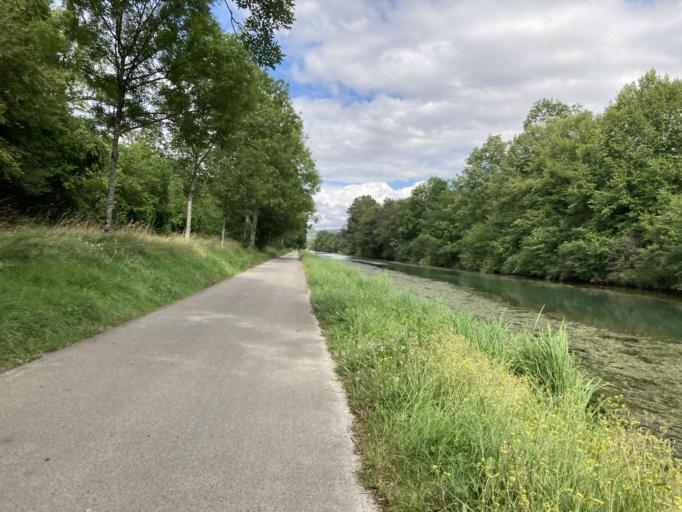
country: FR
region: Bourgogne
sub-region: Departement de la Cote-d'Or
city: Velars-sur-Ouche
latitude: 47.3270
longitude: 4.9356
